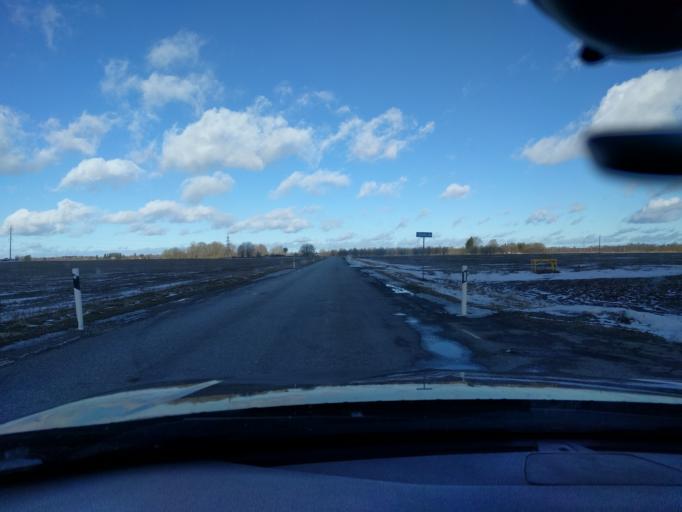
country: EE
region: Harju
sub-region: Raasiku vald
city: Raasiku
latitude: 59.3399
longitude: 25.1525
